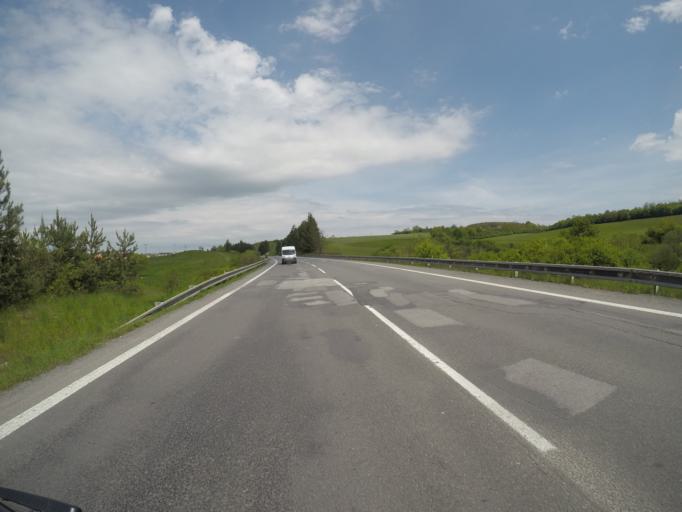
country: SK
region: Banskobystricky
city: Krupina
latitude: 48.4290
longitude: 19.0944
